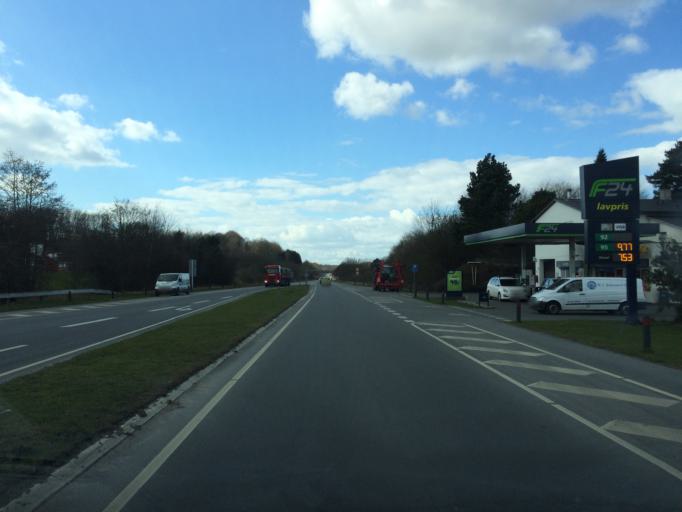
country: DK
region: South Denmark
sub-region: Assens Kommune
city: Vissenbjerg
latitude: 55.3896
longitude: 10.1366
